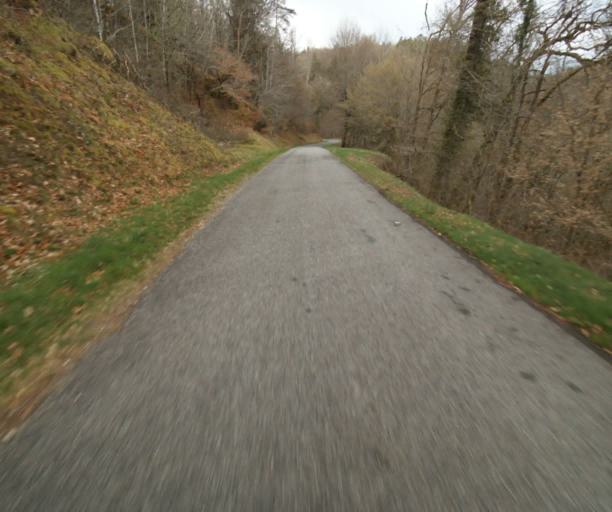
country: FR
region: Limousin
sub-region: Departement de la Correze
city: Argentat
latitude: 45.2272
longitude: 1.9854
